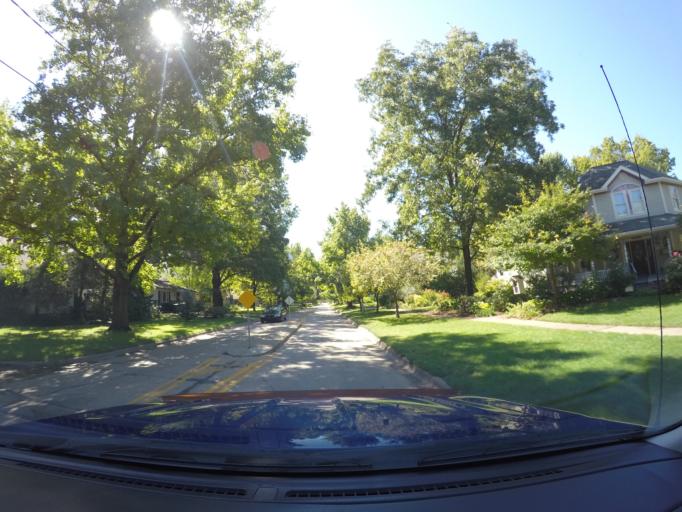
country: US
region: Kansas
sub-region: Douglas County
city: Lawrence
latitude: 38.9536
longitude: -95.2328
